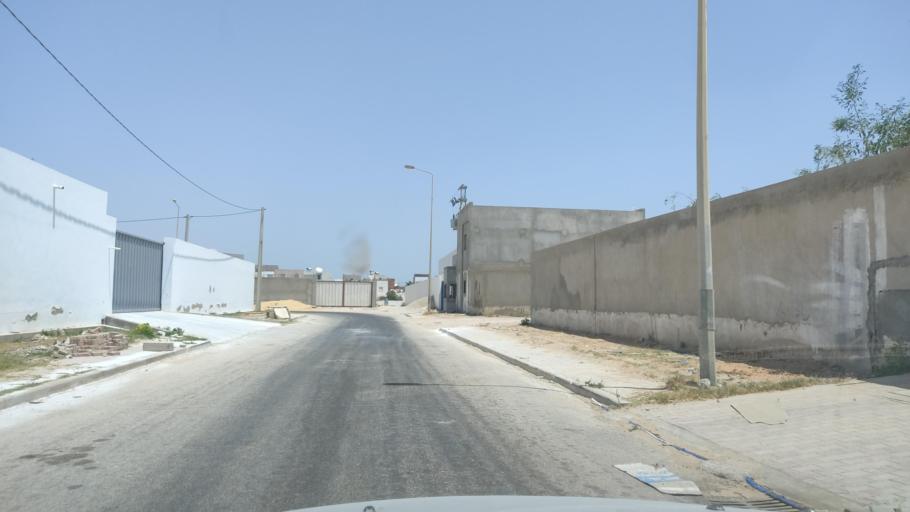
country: TN
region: Safaqis
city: Sfax
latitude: 34.6612
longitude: 10.7010
